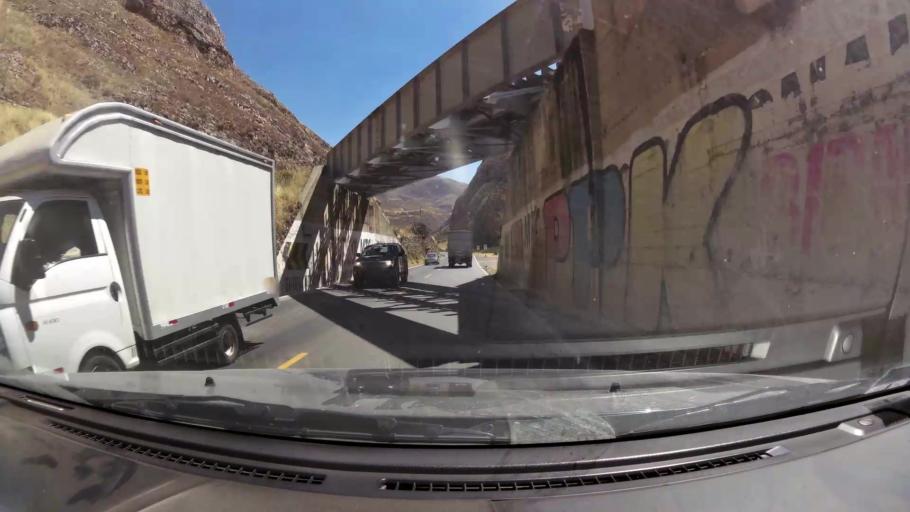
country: PE
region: Junin
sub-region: Provincia de Jauja
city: Parco
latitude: -11.7841
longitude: -75.5695
